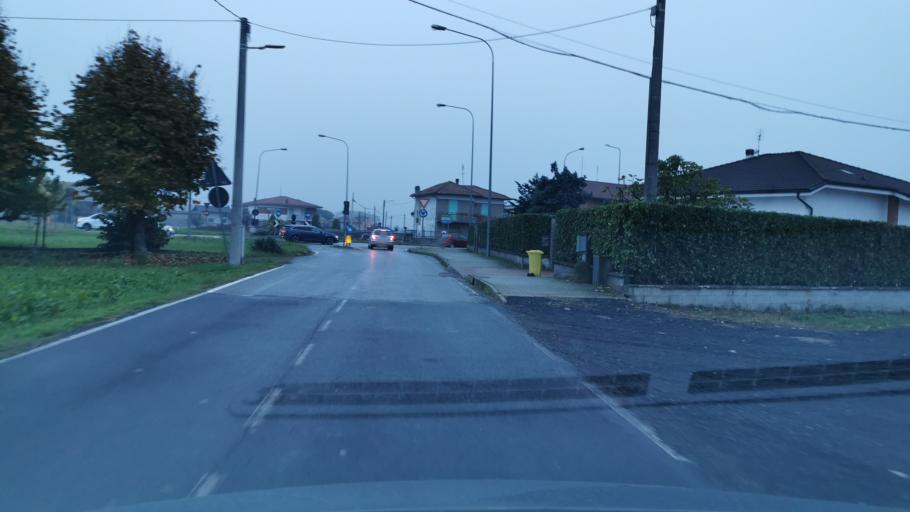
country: IT
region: Piedmont
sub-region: Provincia di Torino
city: Feletto
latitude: 45.2889
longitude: 7.7450
